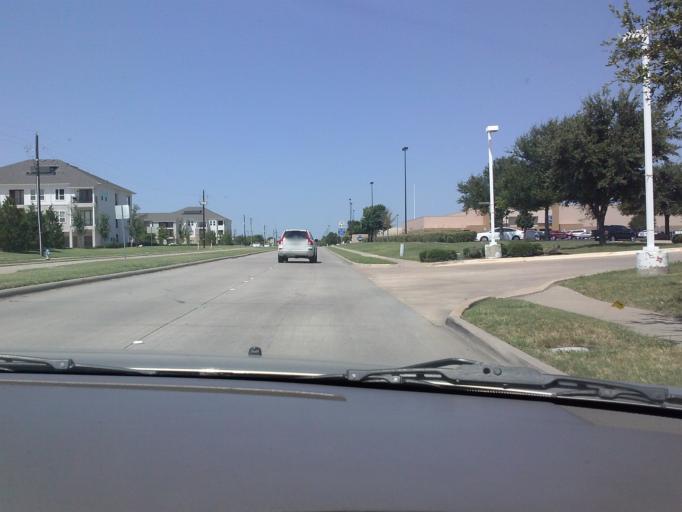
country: US
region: Texas
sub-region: Collin County
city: Frisco
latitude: 33.0944
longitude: -96.7974
